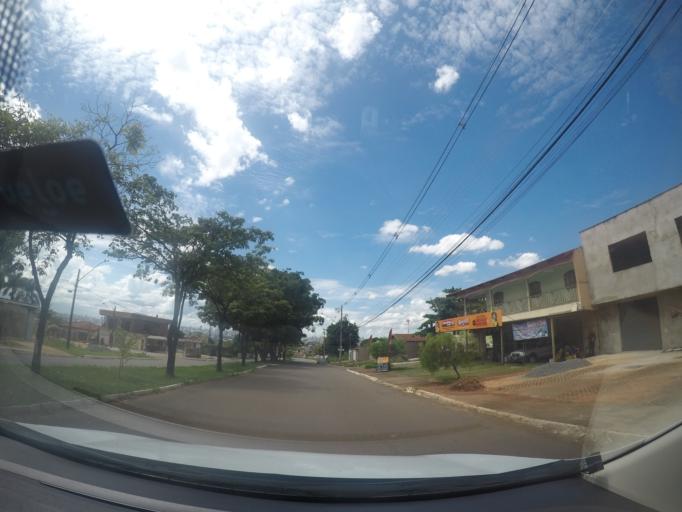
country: BR
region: Goias
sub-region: Goiania
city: Goiania
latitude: -16.6654
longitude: -49.3319
